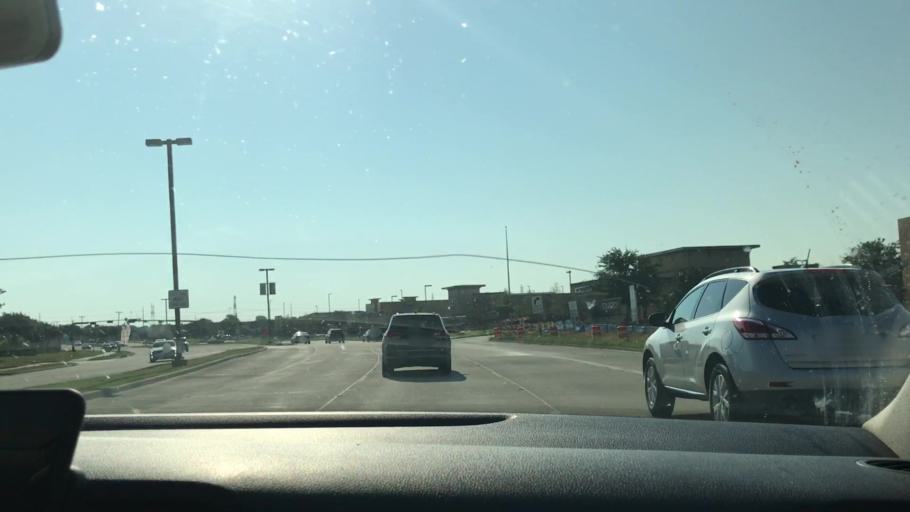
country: US
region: Texas
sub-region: Denton County
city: Lewisville
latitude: 33.0209
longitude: -96.9317
